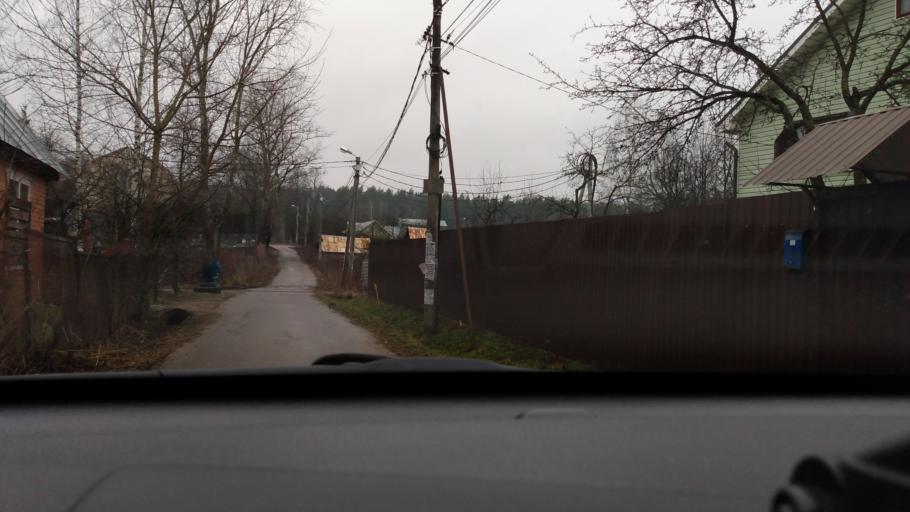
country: RU
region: Moskovskaya
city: Lesnoy Gorodok
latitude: 55.6623
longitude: 37.1744
